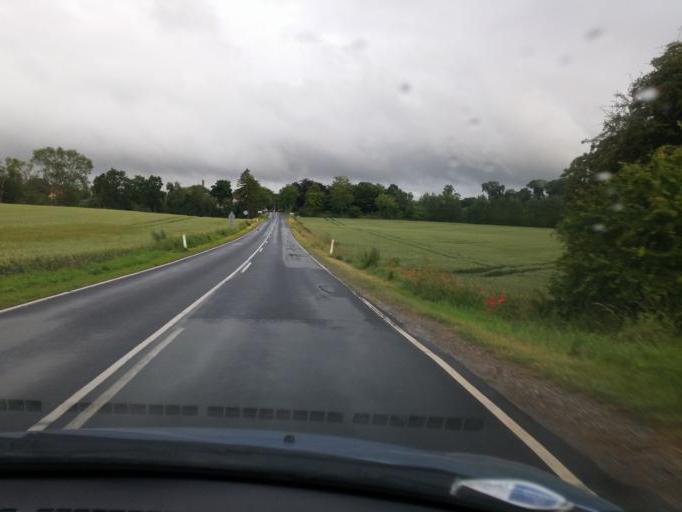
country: DK
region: South Denmark
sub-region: Kerteminde Kommune
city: Kerteminde
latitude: 55.5069
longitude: 10.6501
